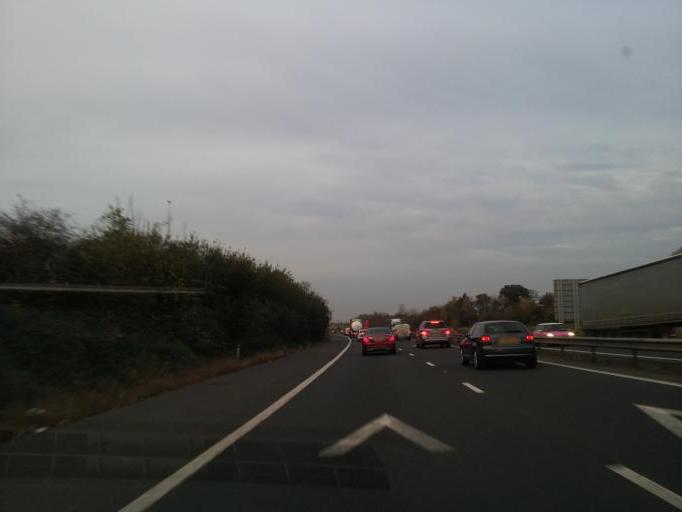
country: GB
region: England
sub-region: Cambridgeshire
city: Duxford
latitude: 52.1171
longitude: 0.1270
